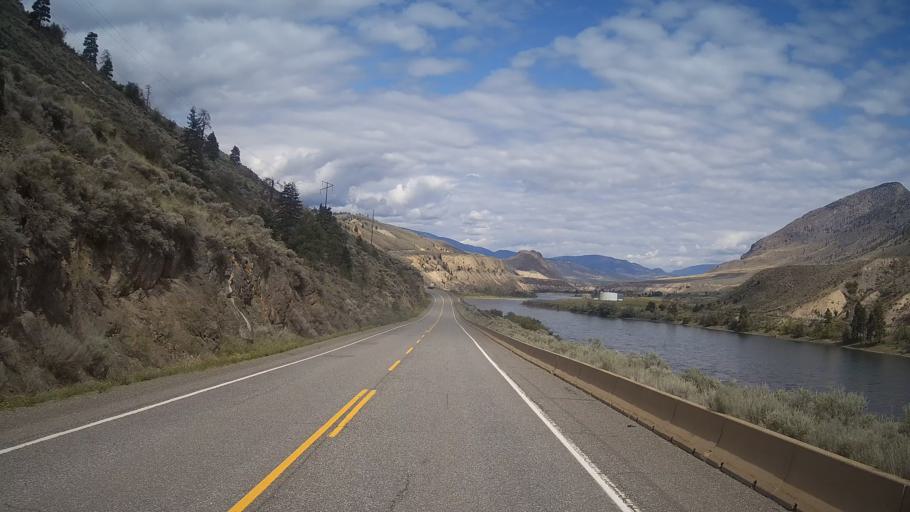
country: CA
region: British Columbia
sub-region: Thompson-Nicola Regional District
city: Ashcroft
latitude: 50.5460
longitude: -121.2921
